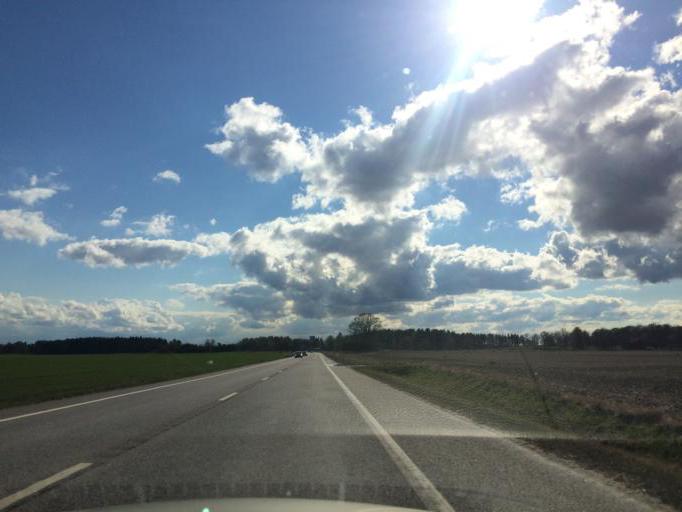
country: SE
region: Soedermanland
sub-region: Eskilstuna Kommun
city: Eskilstuna
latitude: 59.4187
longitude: 16.5942
